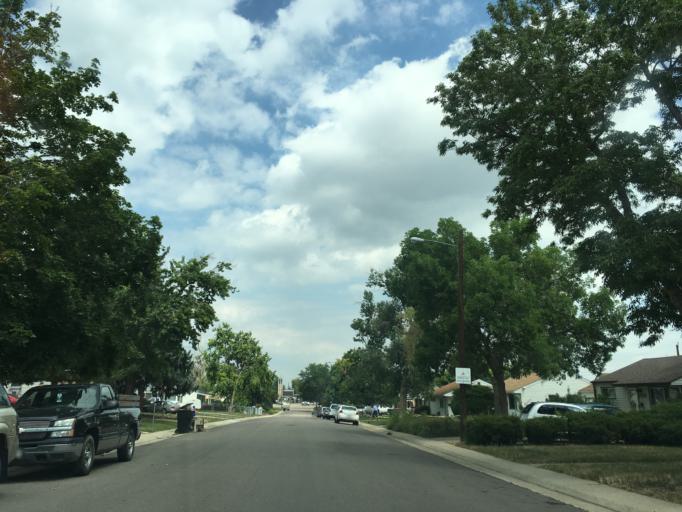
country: US
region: Colorado
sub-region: Arapahoe County
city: Sheridan
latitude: 39.6684
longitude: -105.0261
